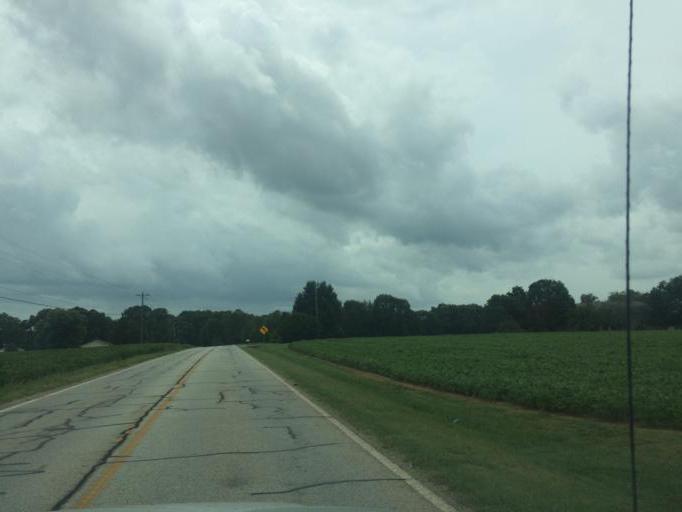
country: US
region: Georgia
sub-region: Hart County
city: Hartwell
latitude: 34.2562
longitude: -82.8994
